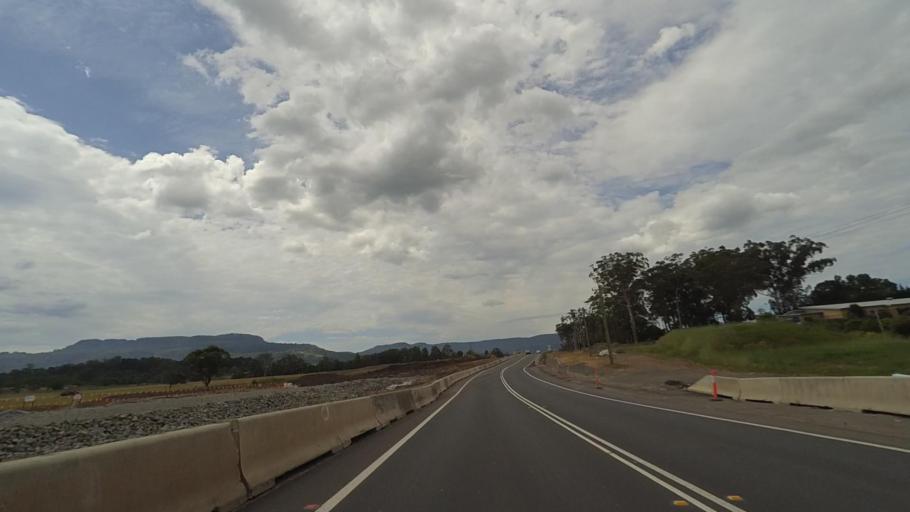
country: AU
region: New South Wales
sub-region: Shoalhaven Shire
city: Berry
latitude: -34.7799
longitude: 150.6810
